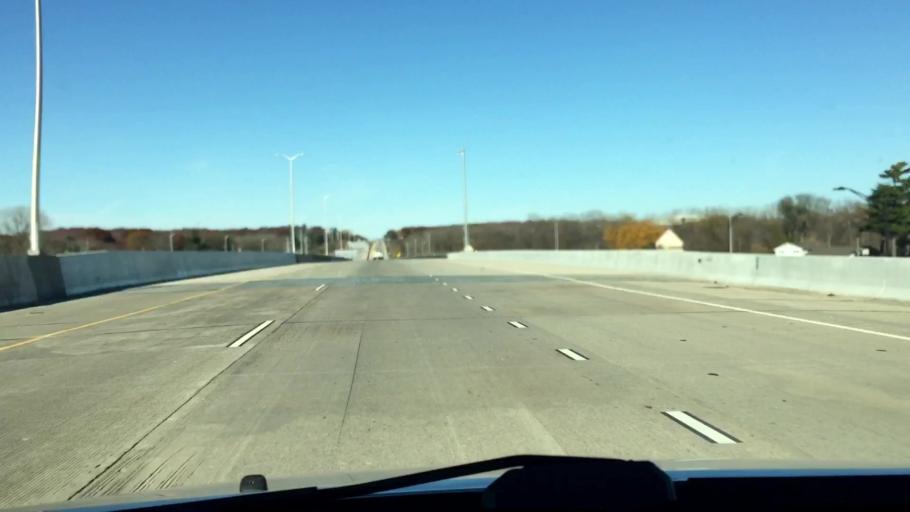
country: US
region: Wisconsin
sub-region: Brown County
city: Howard
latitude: 44.5431
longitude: -88.0879
